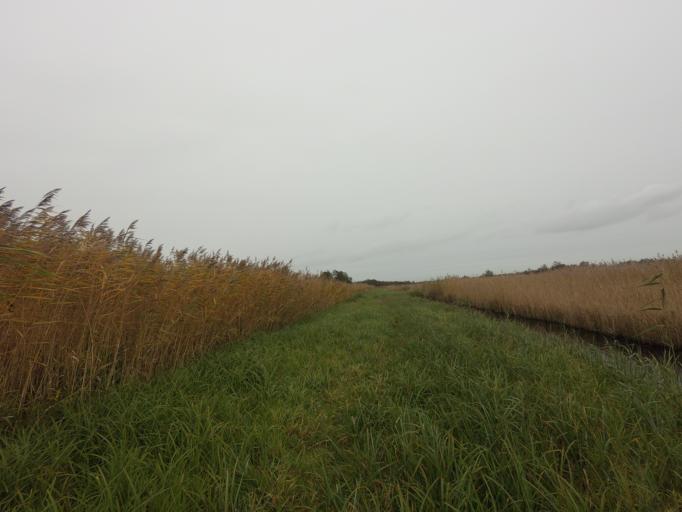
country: NL
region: Overijssel
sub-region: Gemeente Steenwijkerland
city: Oldemarkt
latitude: 52.7778
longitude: 5.9644
